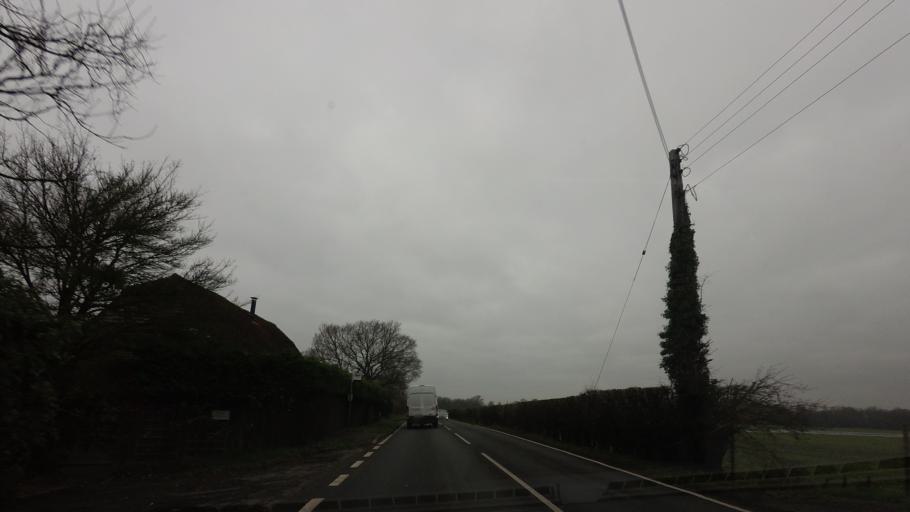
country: GB
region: England
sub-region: Kent
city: Staplehurst
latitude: 51.1413
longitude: 0.5529
